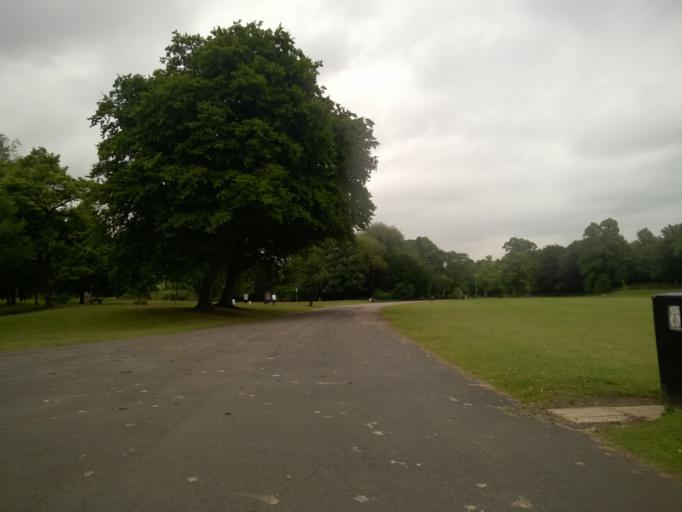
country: GB
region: England
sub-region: City of Leicester
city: Leicester
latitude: 52.6446
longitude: -1.1337
